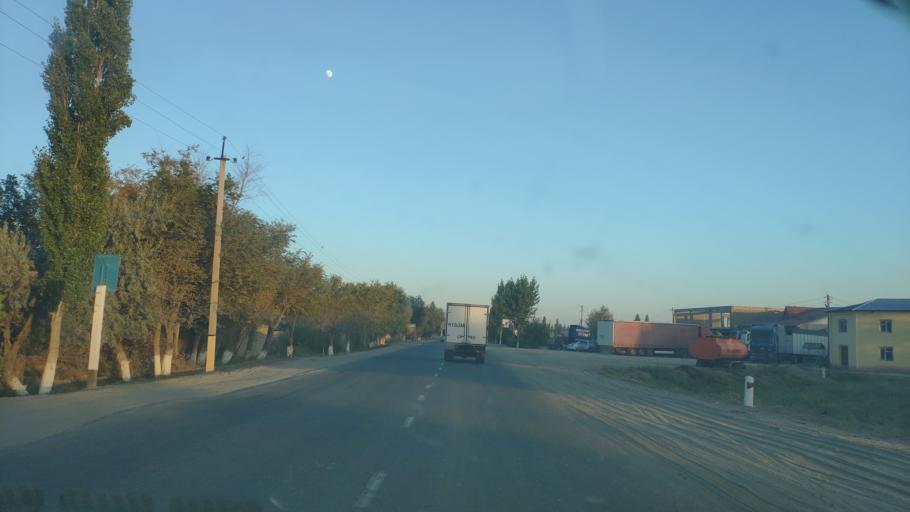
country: UZ
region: Karakalpakstan
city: To'rtko'l Shahri
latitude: 41.5665
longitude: 60.9523
